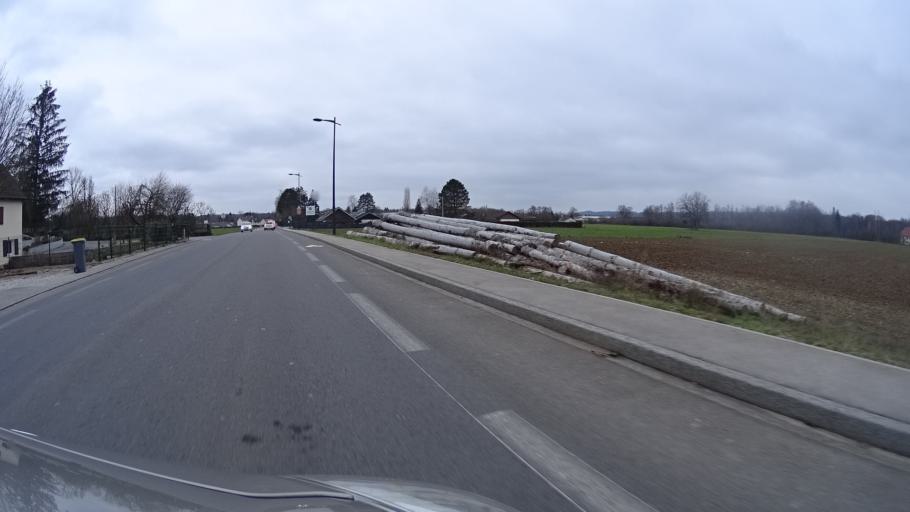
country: FR
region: Franche-Comte
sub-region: Departement du Doubs
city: Saone
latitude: 47.2131
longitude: 6.1066
